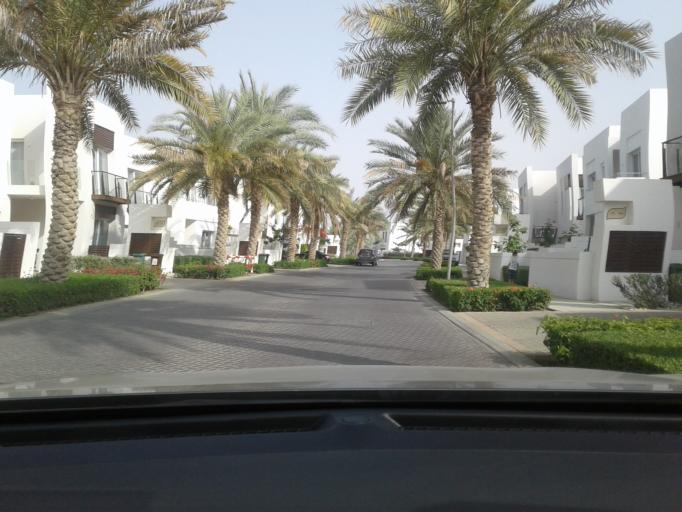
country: OM
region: Muhafazat Masqat
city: As Sib al Jadidah
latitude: 23.6209
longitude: 58.2776
